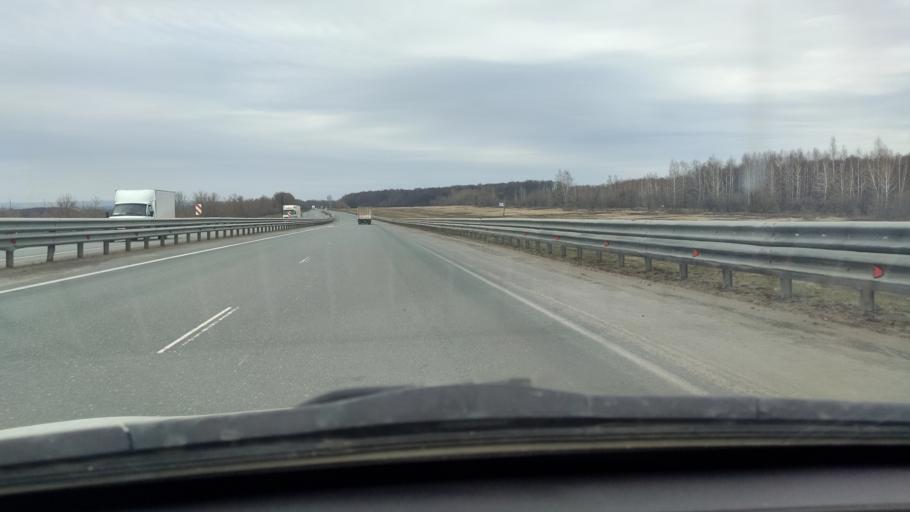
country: RU
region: Samara
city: Zhigulevsk
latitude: 53.2820
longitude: 49.3216
